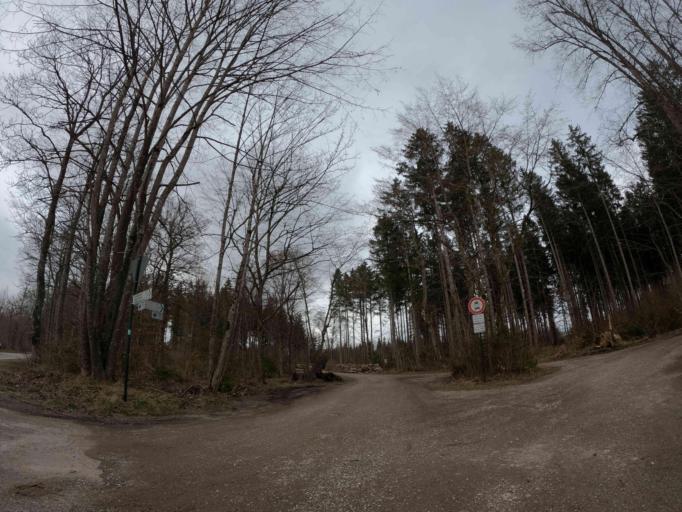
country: DE
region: Bavaria
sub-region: Upper Bavaria
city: Oberhaching
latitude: 48.0142
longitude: 11.5689
